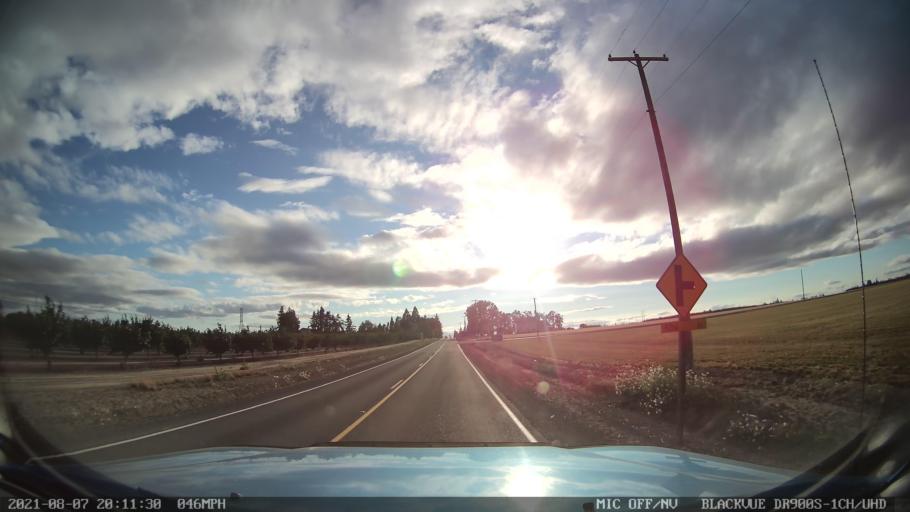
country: US
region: Oregon
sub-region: Marion County
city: Hayesville
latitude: 44.9583
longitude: -122.8917
